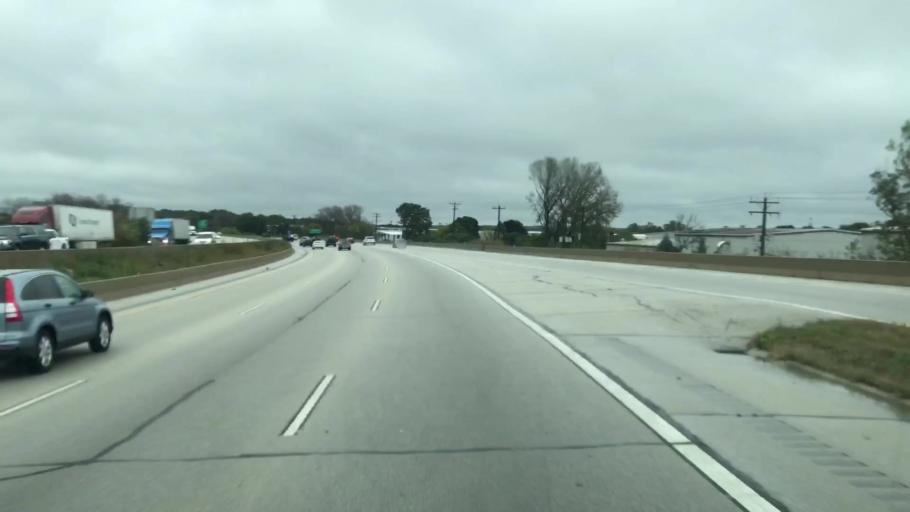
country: US
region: Wisconsin
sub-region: Waukesha County
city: Waukesha
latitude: 43.0391
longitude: -88.1773
